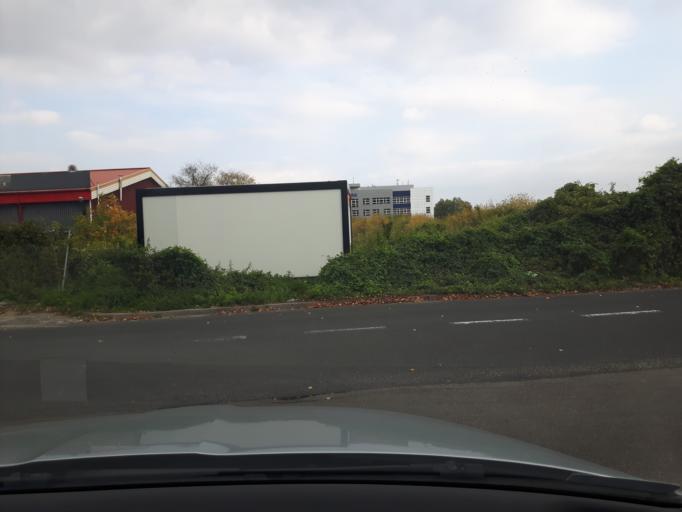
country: PL
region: Masovian Voivodeship
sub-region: Warszawa
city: Wlochy
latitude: 52.2000
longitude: 20.9380
